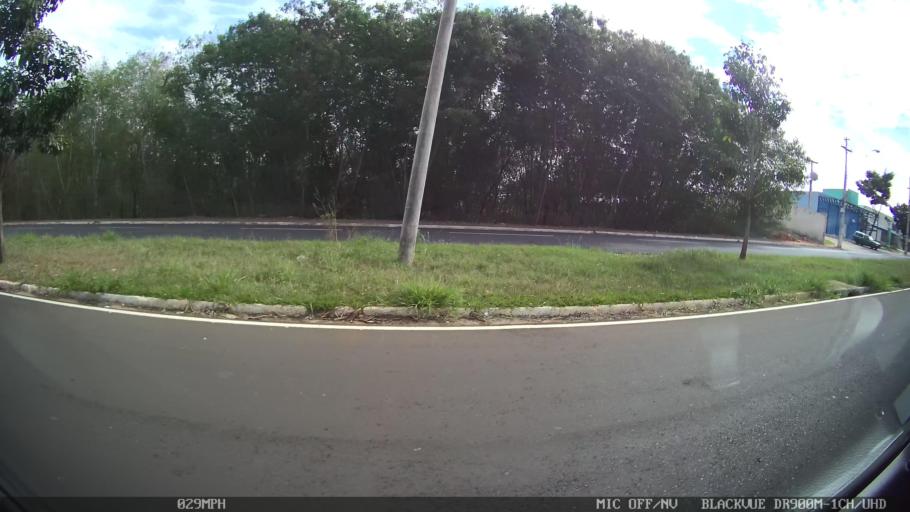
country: BR
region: Sao Paulo
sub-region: Catanduva
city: Catanduva
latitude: -21.1489
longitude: -48.9496
